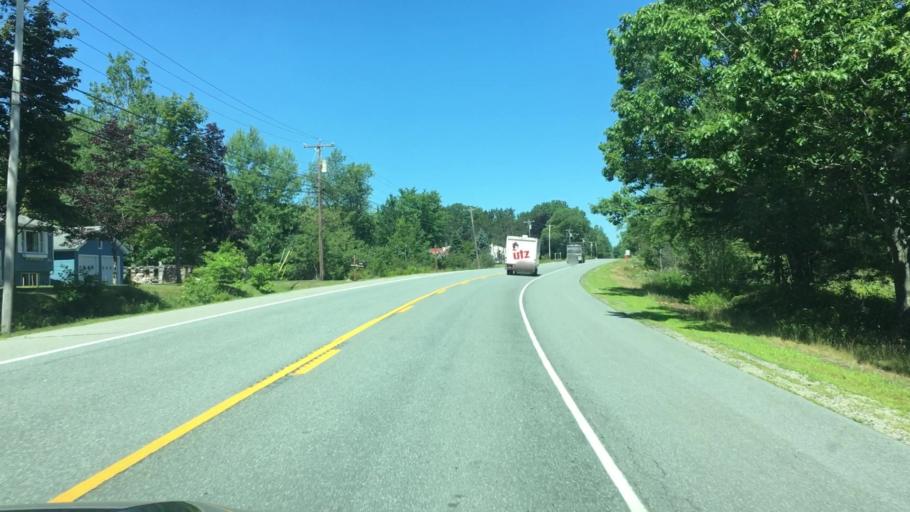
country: US
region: Maine
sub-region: Hancock County
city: Orland
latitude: 44.5610
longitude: -68.7111
